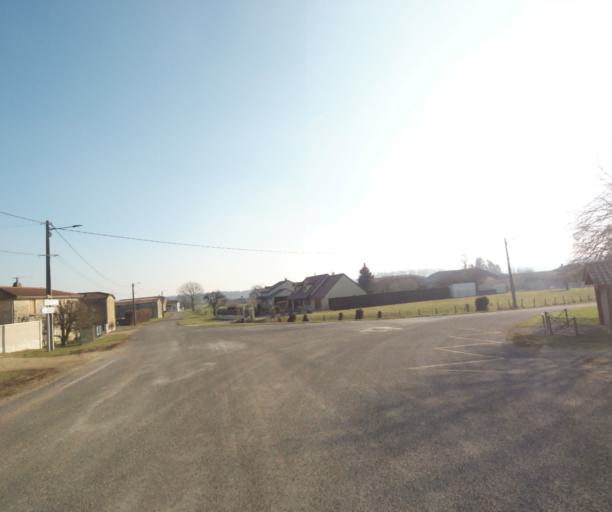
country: FR
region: Champagne-Ardenne
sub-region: Departement de la Haute-Marne
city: Bienville
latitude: 48.5057
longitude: 5.0355
